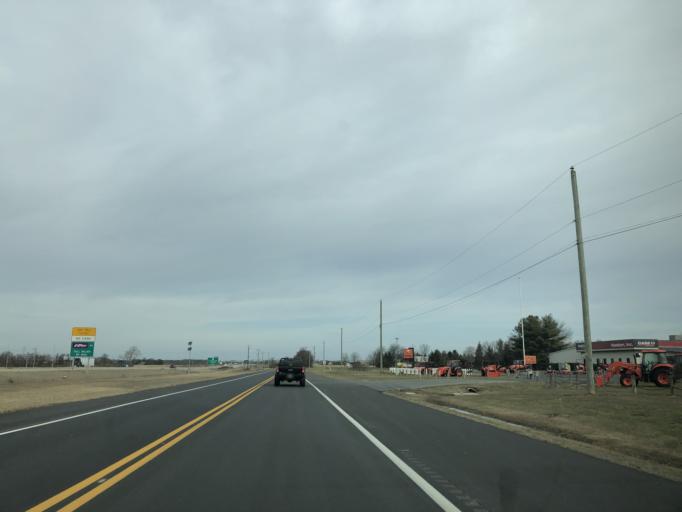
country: US
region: Delaware
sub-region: New Castle County
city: Middletown
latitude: 39.4246
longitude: -75.7621
